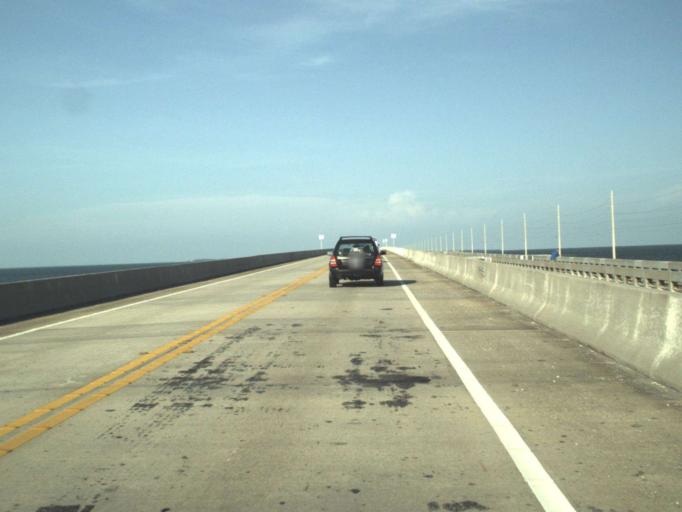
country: US
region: Florida
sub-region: Monroe County
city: Marathon
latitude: 24.7912
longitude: -80.8839
